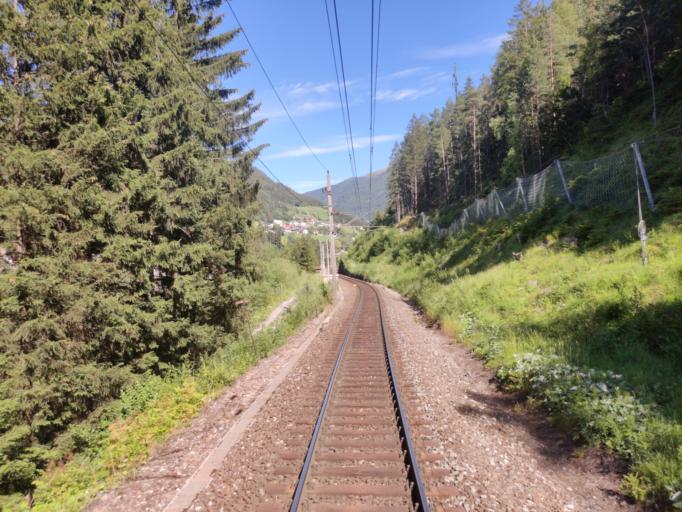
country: AT
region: Tyrol
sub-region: Politischer Bezirk Landeck
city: Strengen
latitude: 47.1272
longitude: 10.4521
